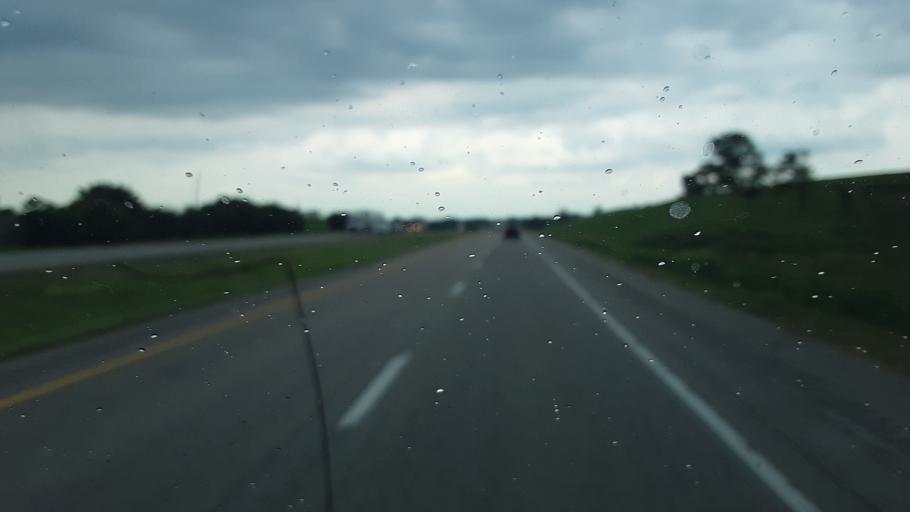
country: US
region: Iowa
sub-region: Pottawattamie County
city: Council Bluffs
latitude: 41.3641
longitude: -95.6878
